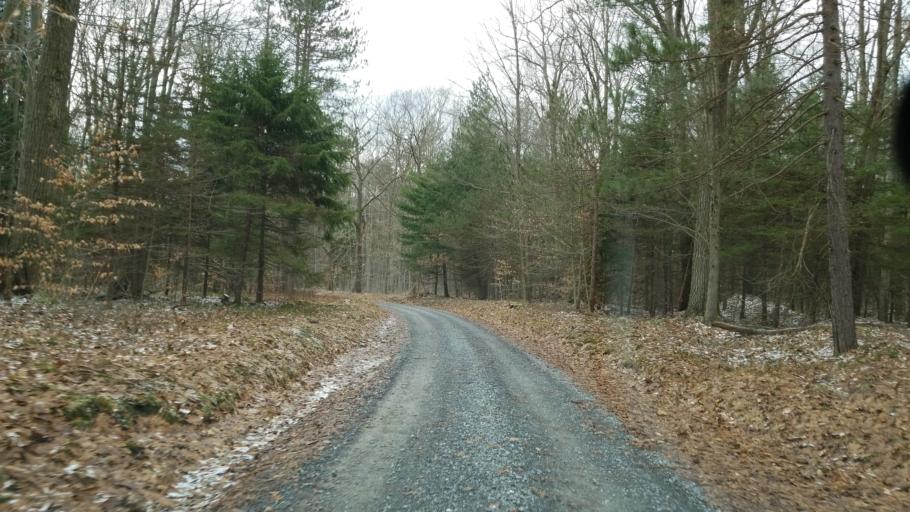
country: US
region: Pennsylvania
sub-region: Clearfield County
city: Clearfield
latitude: 41.1409
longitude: -78.5405
